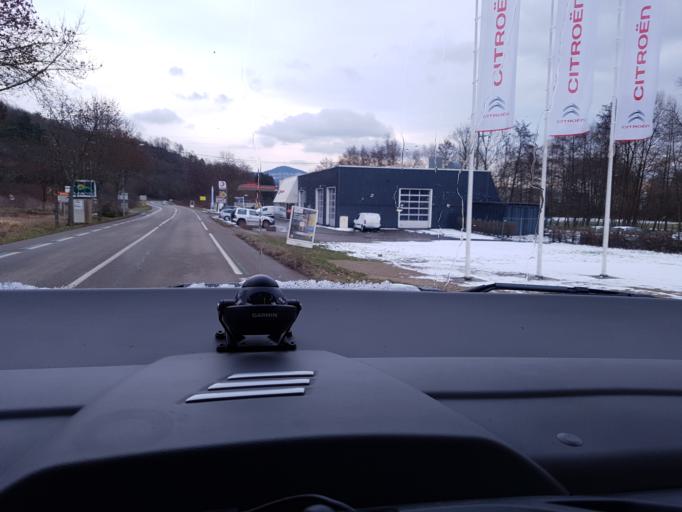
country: FR
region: Alsace
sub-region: Departement du Bas-Rhin
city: Ville
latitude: 48.3406
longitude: 7.3123
